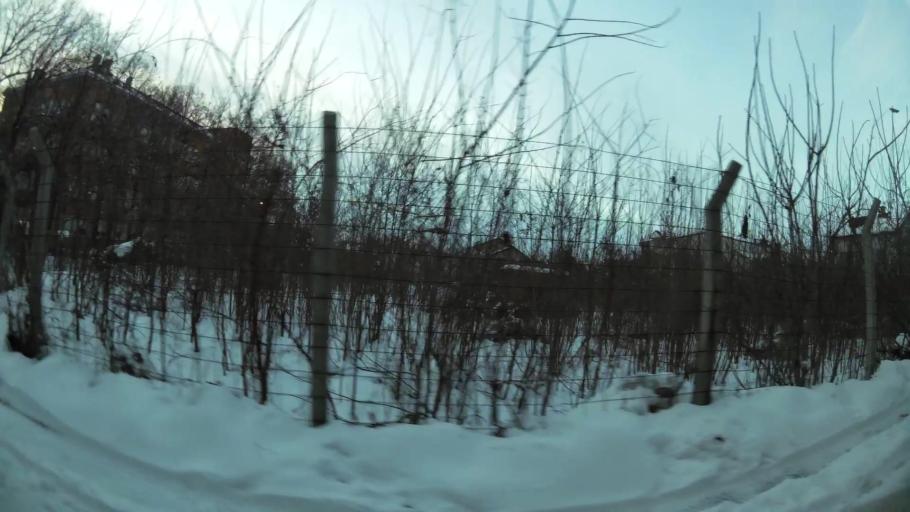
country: RS
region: Central Serbia
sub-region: Belgrade
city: Palilula
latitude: 44.8006
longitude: 20.5018
